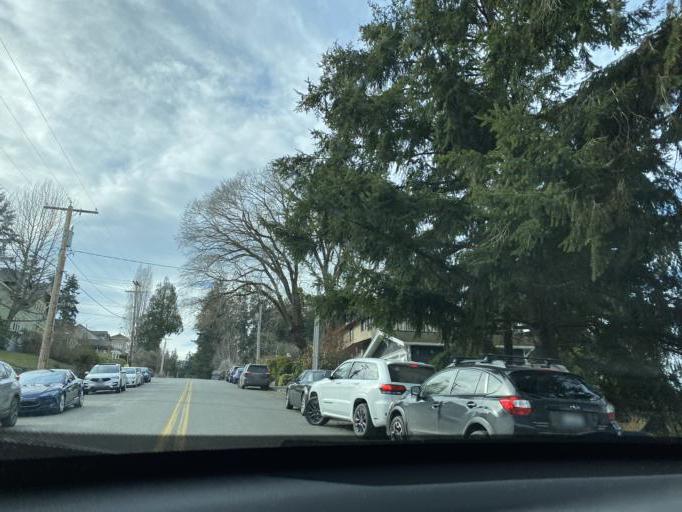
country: US
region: Washington
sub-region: Island County
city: Langley
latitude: 48.0409
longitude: -122.4111
